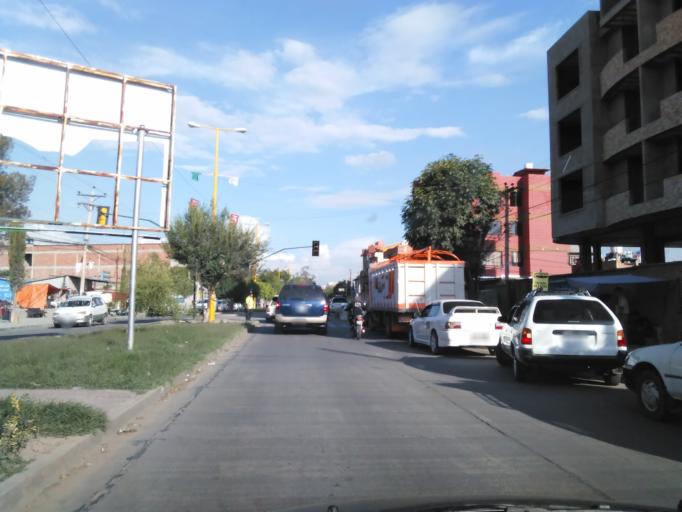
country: BO
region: Cochabamba
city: Cochabamba
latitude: -17.3452
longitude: -66.2046
